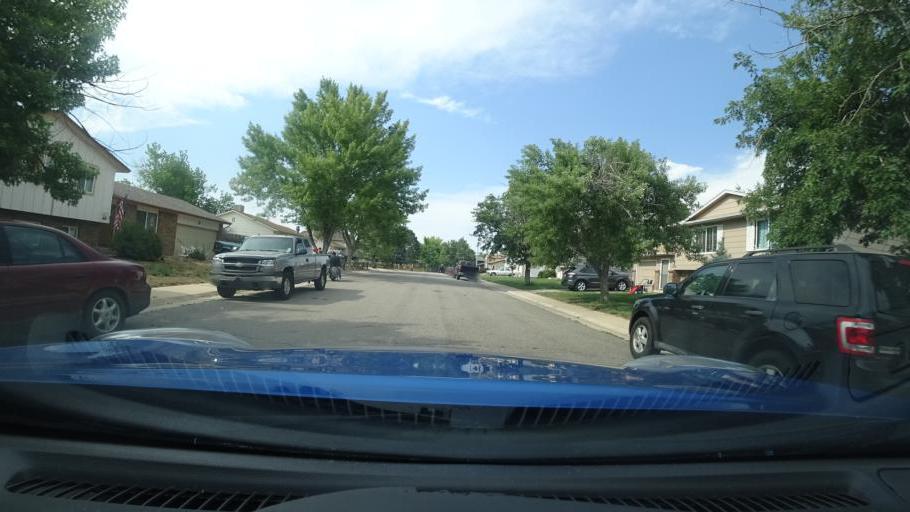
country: US
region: Colorado
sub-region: Adams County
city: Aurora
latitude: 39.6877
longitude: -104.7981
